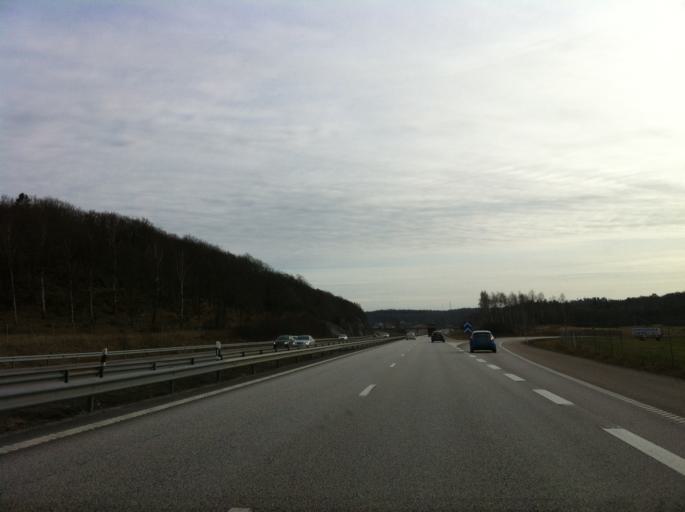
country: SE
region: Vaestra Goetaland
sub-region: Molndal
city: Kallered
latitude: 57.5873
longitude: 12.0639
